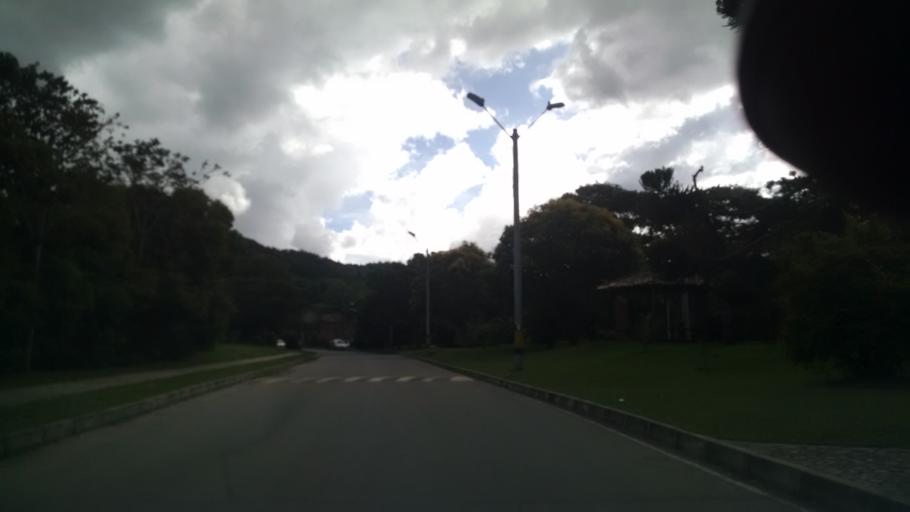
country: CO
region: Antioquia
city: El Retiro
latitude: 6.0579
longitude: -75.5063
